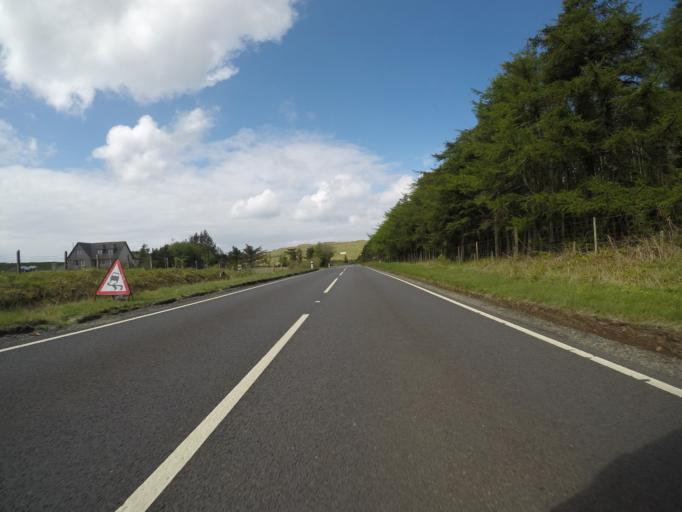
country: GB
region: Scotland
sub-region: Highland
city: Portree
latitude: 57.5280
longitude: -6.3479
